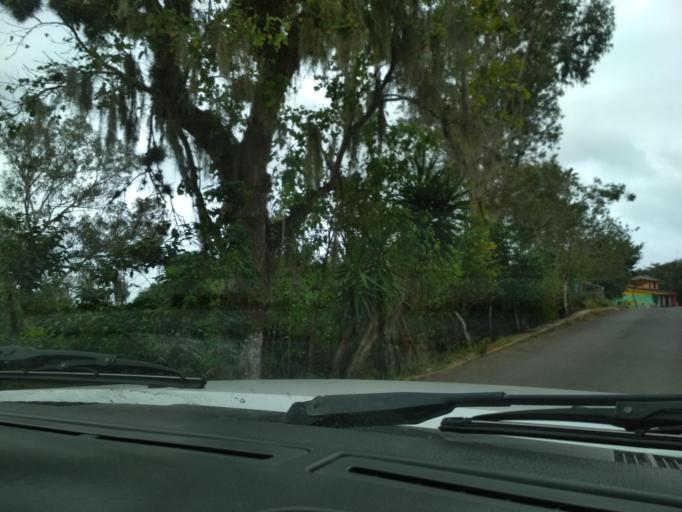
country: MX
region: Veracruz
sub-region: Emiliano Zapata
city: Dos Rios
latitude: 19.5381
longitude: -96.8001
